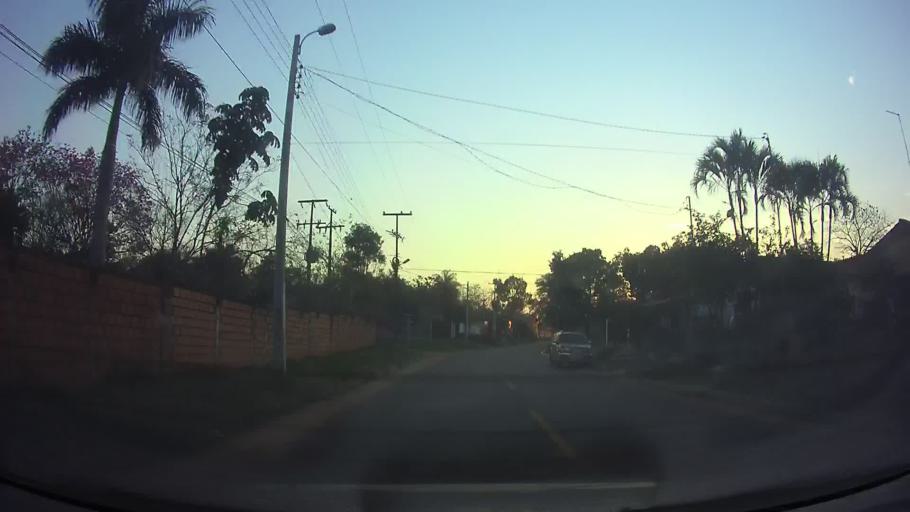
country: PY
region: Central
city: Limpio
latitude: -25.2375
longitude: -57.5002
